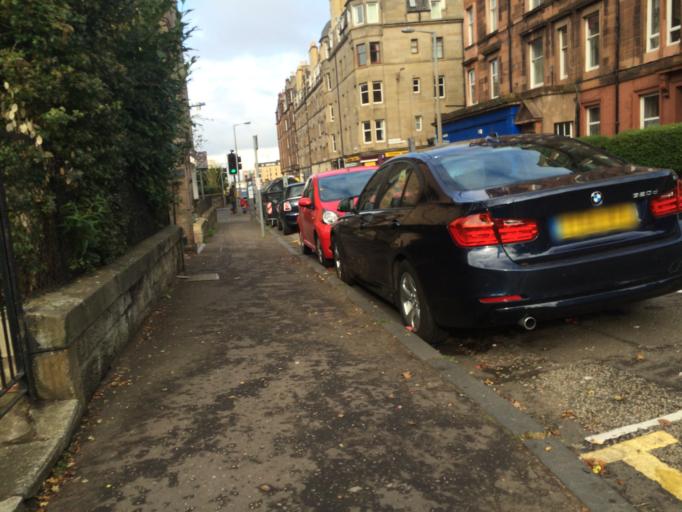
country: GB
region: Scotland
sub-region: Edinburgh
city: Edinburgh
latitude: 55.9394
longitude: -3.2117
